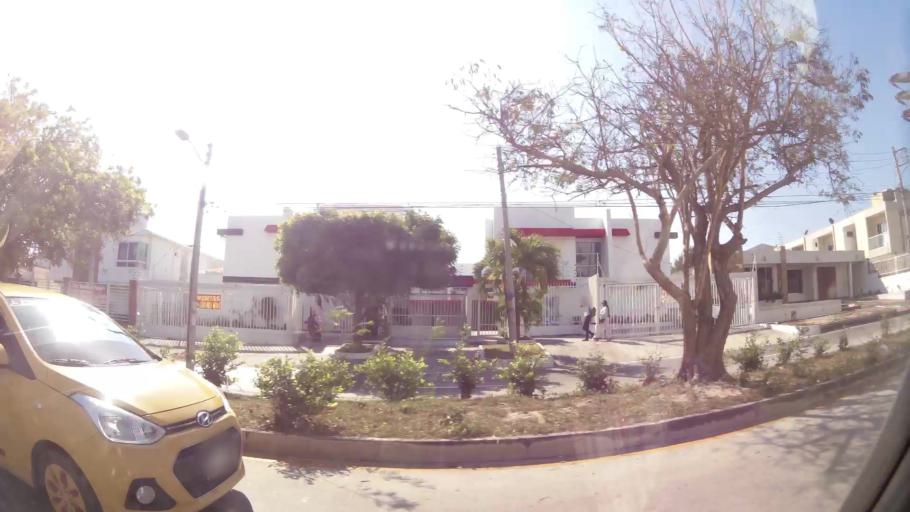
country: CO
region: Atlantico
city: Barranquilla
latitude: 10.9924
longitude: -74.8213
